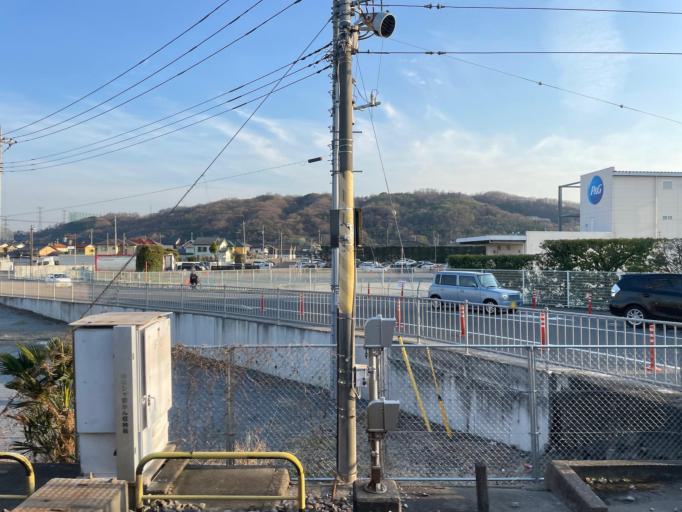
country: JP
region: Gunma
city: Takasaki
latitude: 36.3378
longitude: 138.9622
